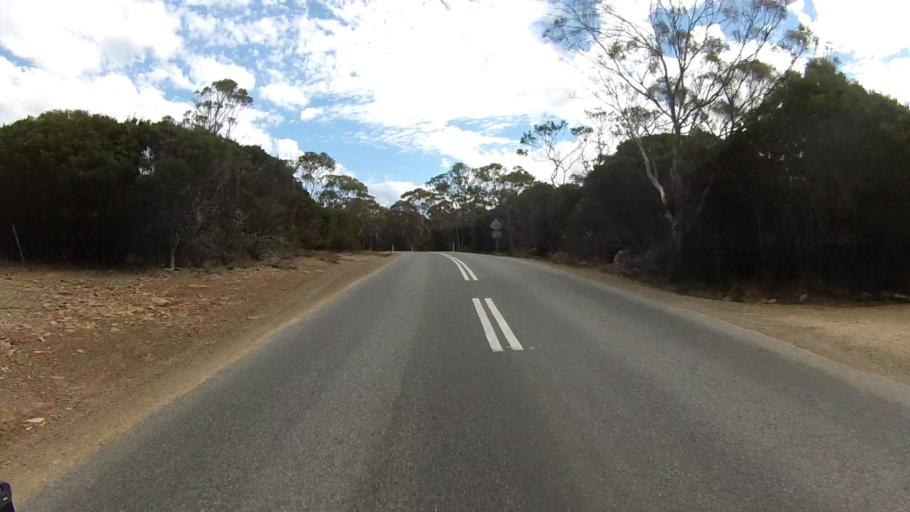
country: AU
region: Tasmania
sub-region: Break O'Day
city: St Helens
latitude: -41.9772
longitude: 148.1452
